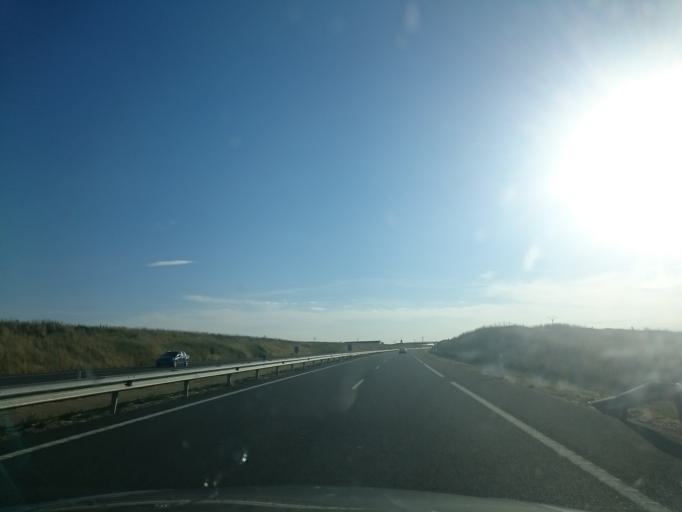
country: ES
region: Castille and Leon
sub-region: Provincia de Palencia
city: Villaherreros
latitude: 42.3938
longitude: -4.4395
